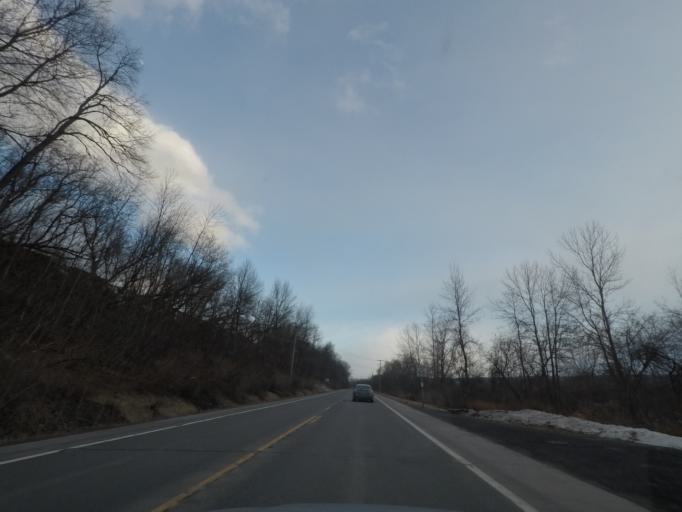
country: US
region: New York
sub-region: Herkimer County
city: Frankfort
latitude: 43.0413
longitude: -75.0584
